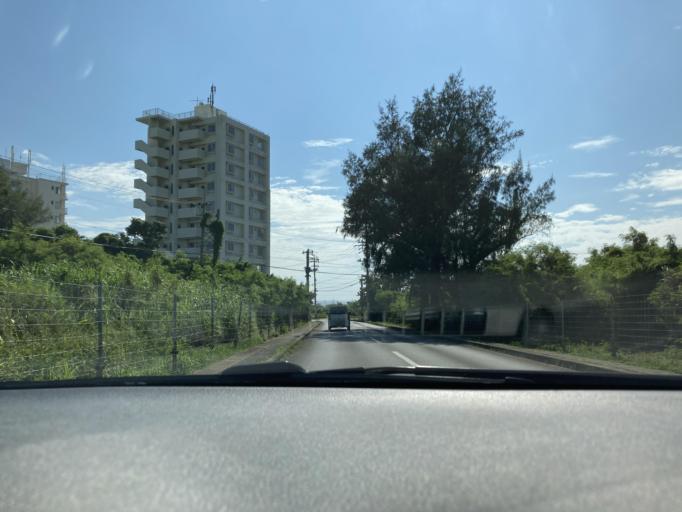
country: JP
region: Okinawa
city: Chatan
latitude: 26.3685
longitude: 127.7434
